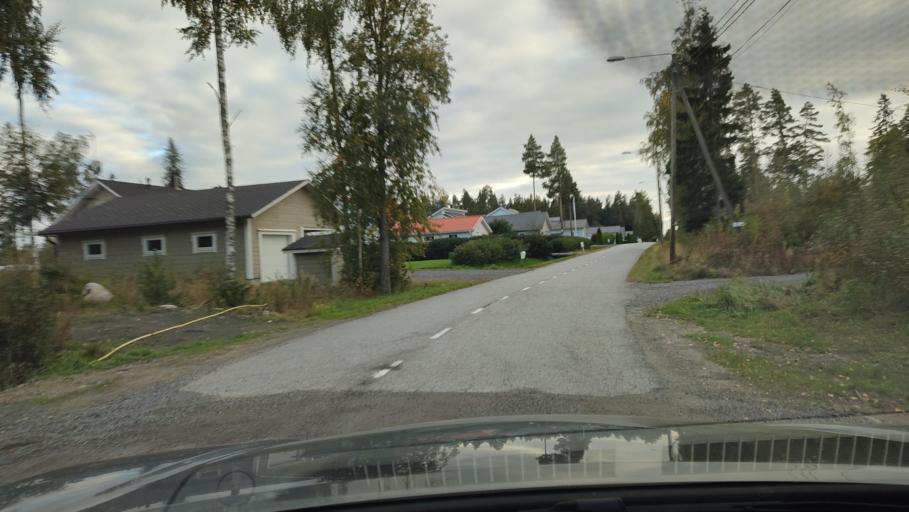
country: FI
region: Ostrobothnia
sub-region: Sydosterbotten
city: Kristinestad
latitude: 62.2567
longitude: 21.3841
